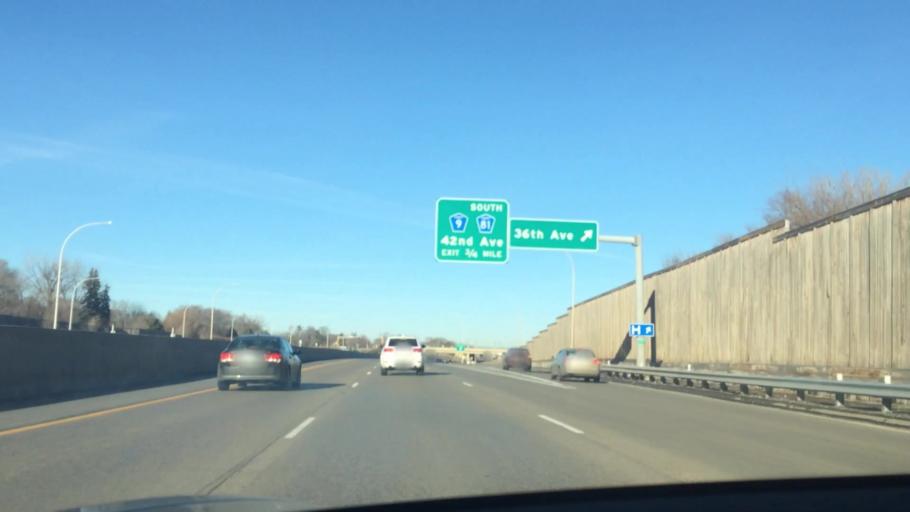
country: US
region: Minnesota
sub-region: Hennepin County
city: Golden Valley
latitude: 45.0171
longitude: -93.3493
